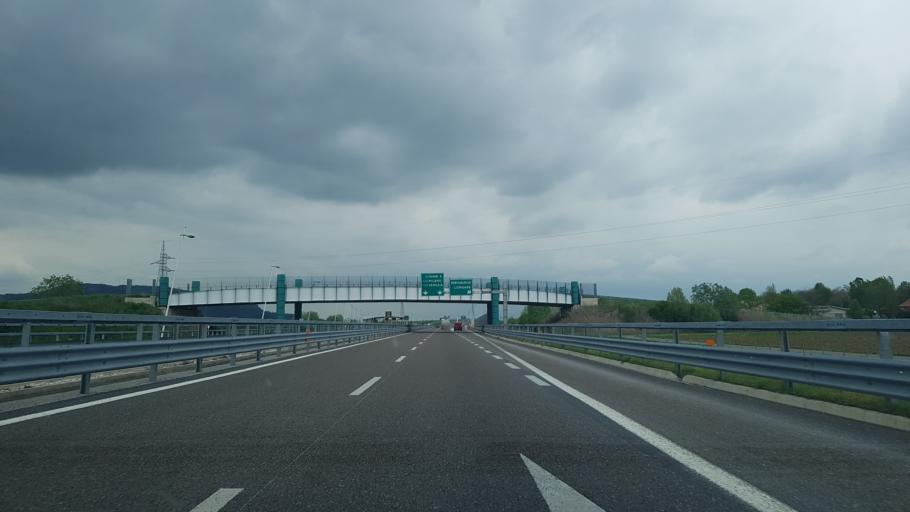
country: IT
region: Veneto
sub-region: Provincia di Vicenza
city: Villaganzerla
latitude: 45.4429
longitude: 11.6334
